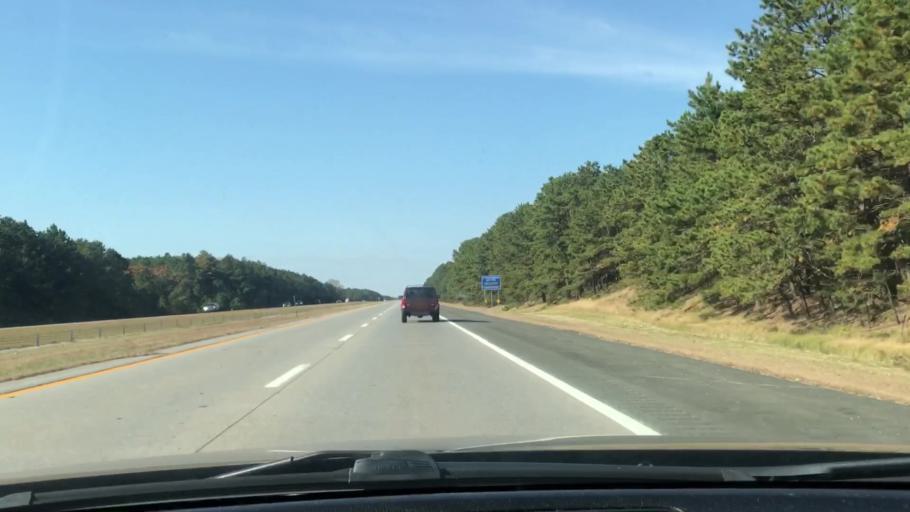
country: US
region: New York
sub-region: Suffolk County
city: East Quogue
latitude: 40.8762
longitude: -72.5613
